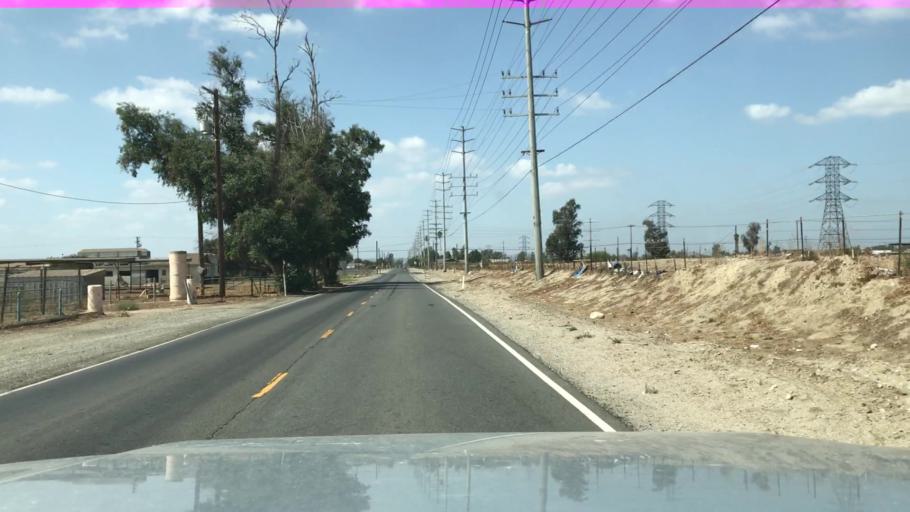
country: US
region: California
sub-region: San Bernardino County
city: Chino
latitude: 33.9978
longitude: -117.6168
